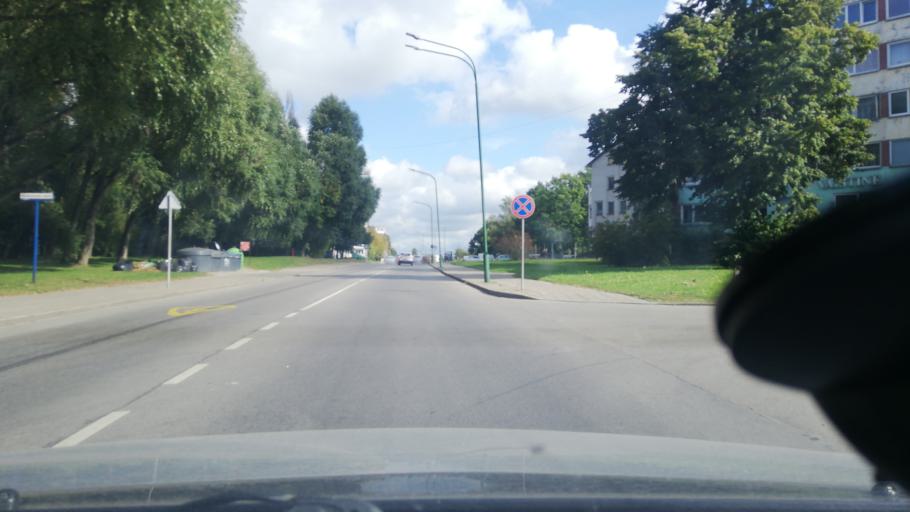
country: LT
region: Klaipedos apskritis
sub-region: Klaipeda
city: Klaipeda
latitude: 55.6842
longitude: 21.1774
